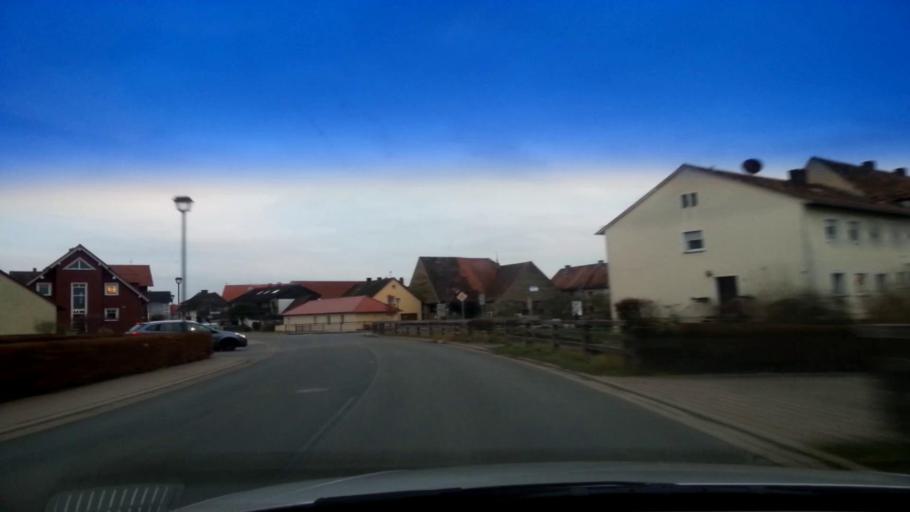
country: DE
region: Bavaria
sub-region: Upper Franconia
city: Pommersfelden
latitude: 49.7742
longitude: 10.8025
